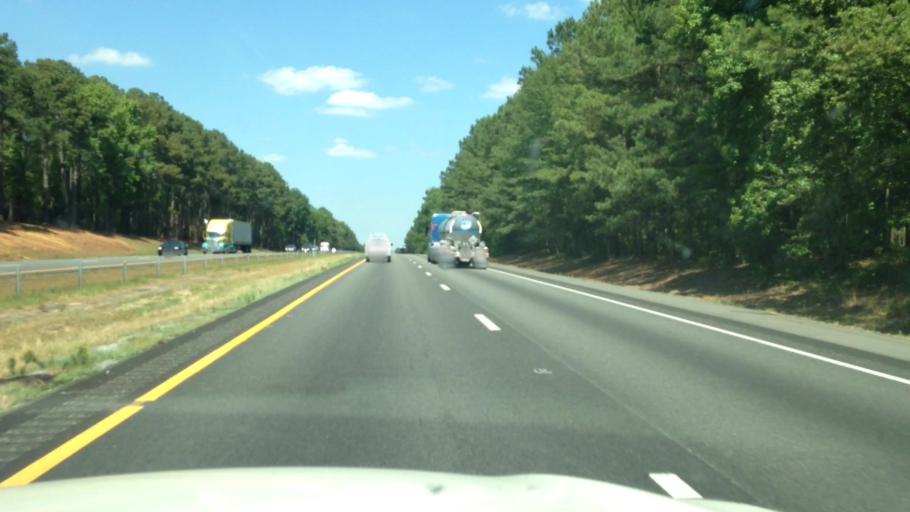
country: US
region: North Carolina
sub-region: Johnston County
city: Four Oaks
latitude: 35.4213
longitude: -78.4524
